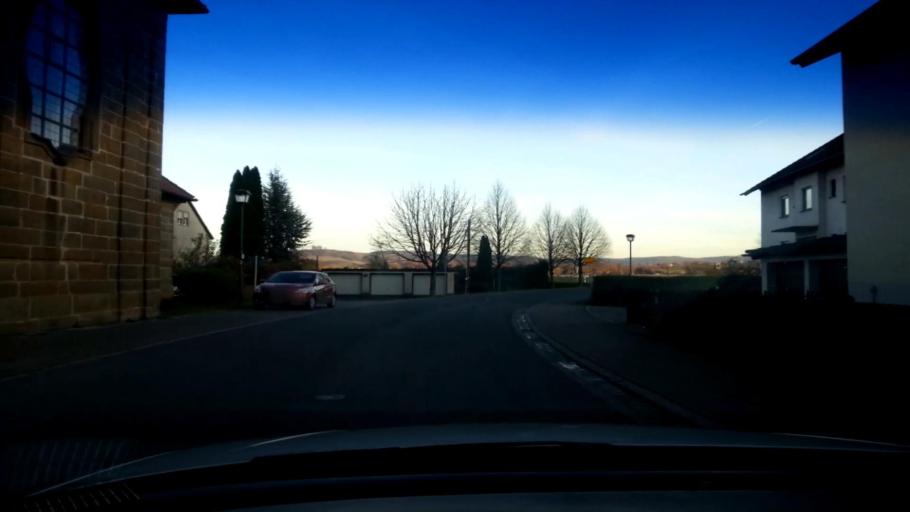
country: DE
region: Bavaria
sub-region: Upper Franconia
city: Ebensfeld
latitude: 50.0654
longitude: 10.9416
